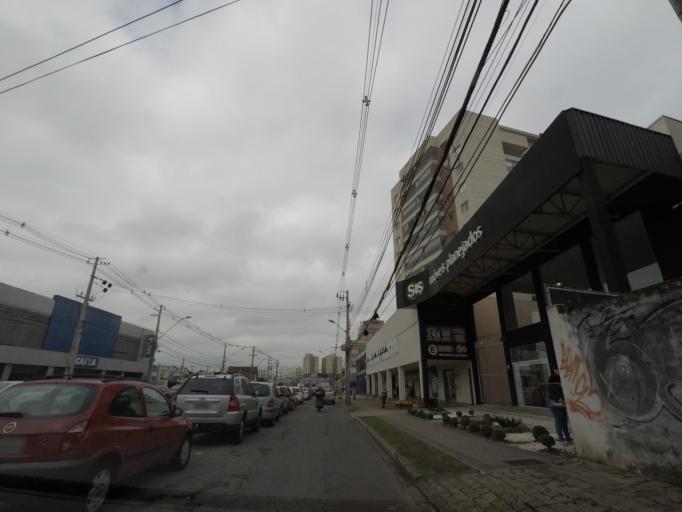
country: BR
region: Parana
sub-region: Curitiba
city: Curitiba
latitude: -25.4856
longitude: -49.2942
